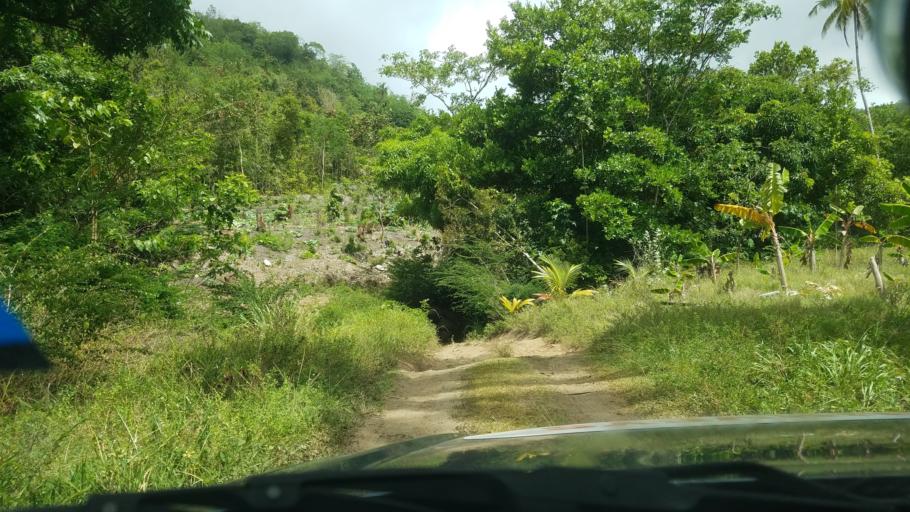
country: LC
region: Dennery Quarter
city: Dennery
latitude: 13.9864
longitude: -60.8888
